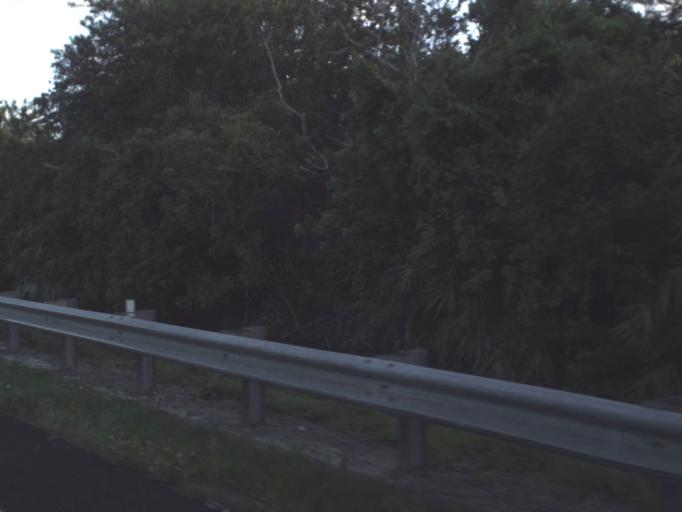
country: US
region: Florida
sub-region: Brevard County
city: South Patrick Shores
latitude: 28.2459
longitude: -80.6798
